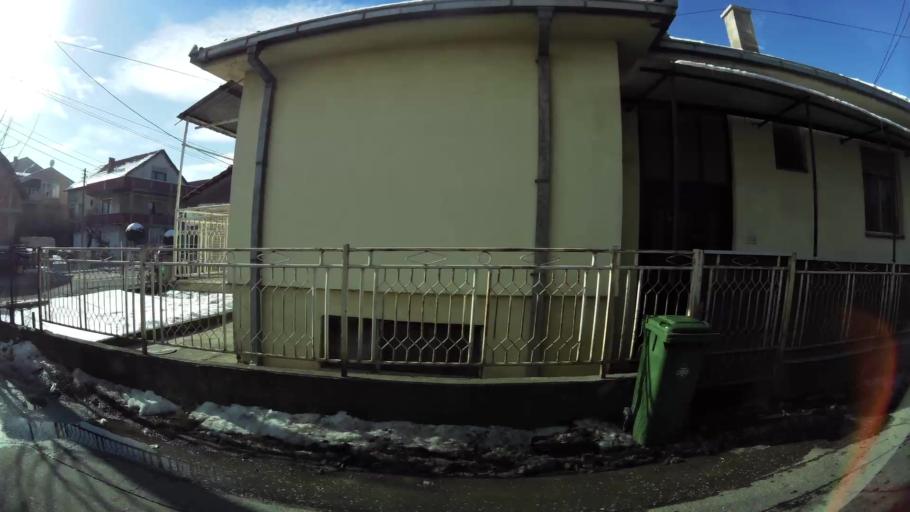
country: MK
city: Krushopek
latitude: 42.0091
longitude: 21.3575
